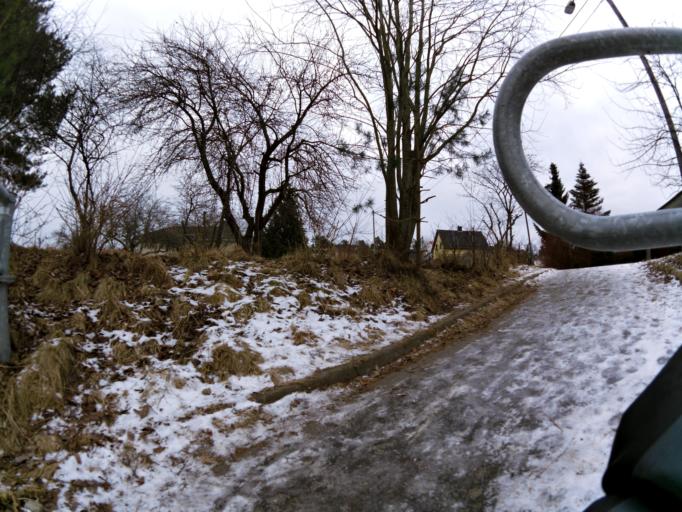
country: NO
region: Ostfold
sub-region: Fredrikstad
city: Fredrikstad
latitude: 59.2042
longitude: 10.8822
